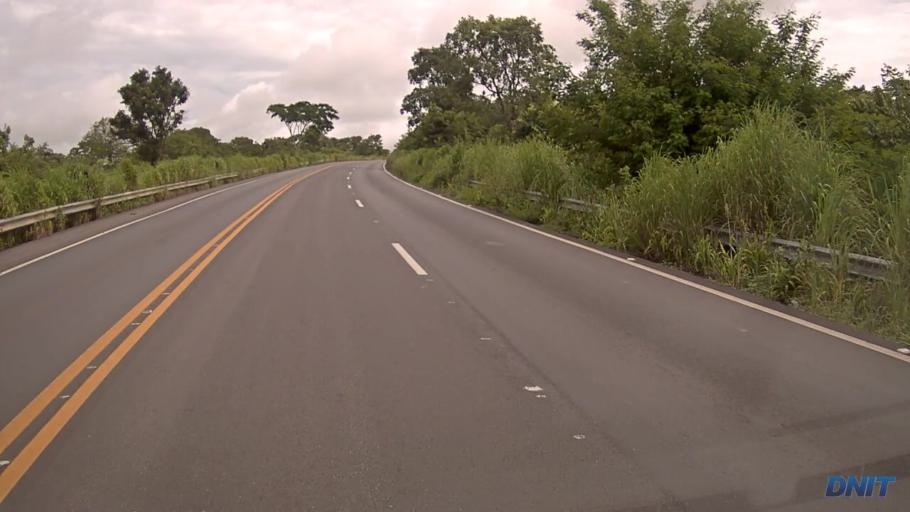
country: BR
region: Goias
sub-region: Posse
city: Posse
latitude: -14.3360
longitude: -46.4372
